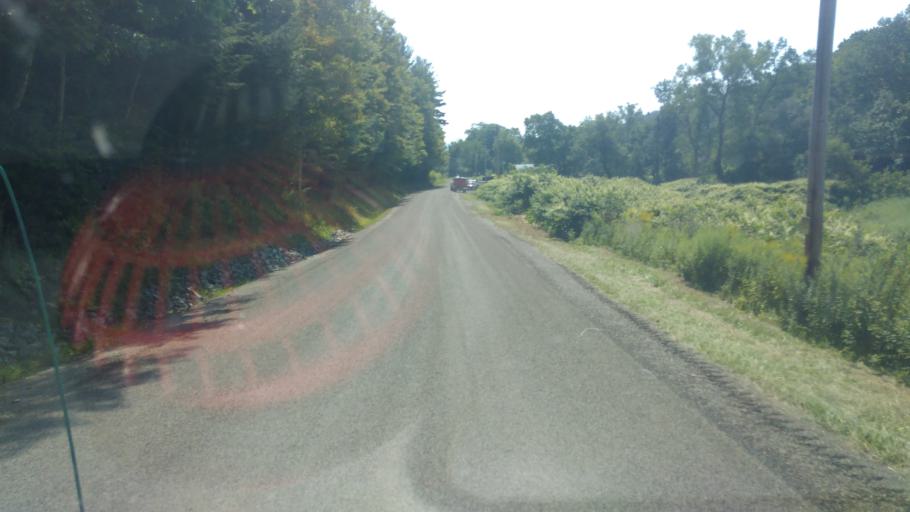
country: US
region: New York
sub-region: Steuben County
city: Canisteo
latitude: 42.3146
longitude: -77.6045
